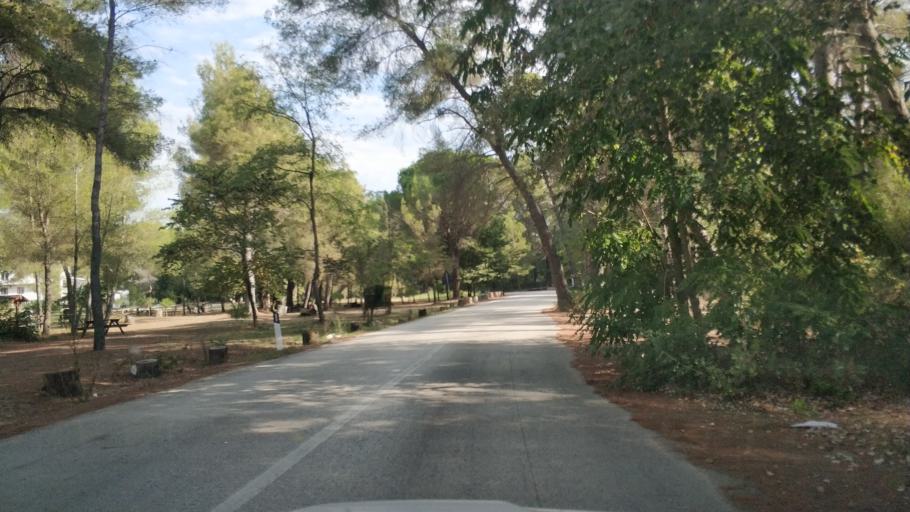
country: AL
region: Fier
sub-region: Rrethi i Lushnjes
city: Divjake
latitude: 40.9890
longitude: 19.4850
